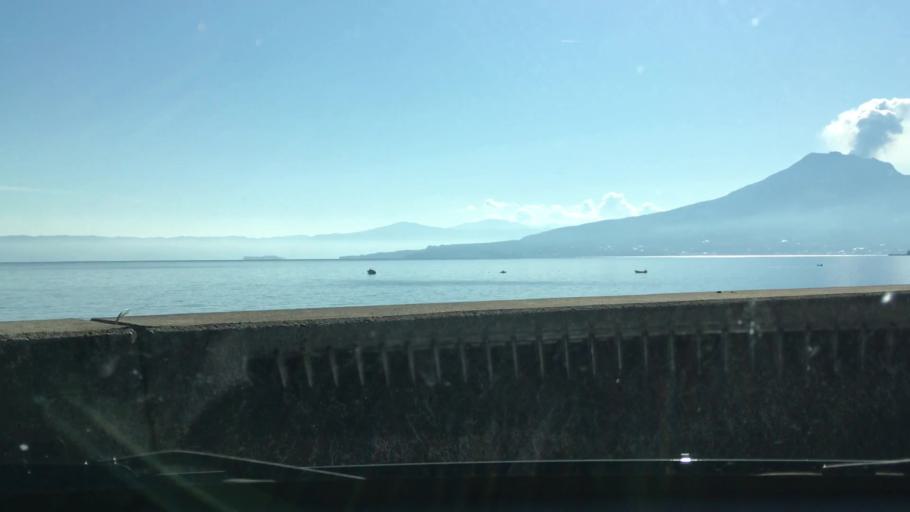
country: JP
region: Kagoshima
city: Kajiki
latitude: 31.6826
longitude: 130.6096
